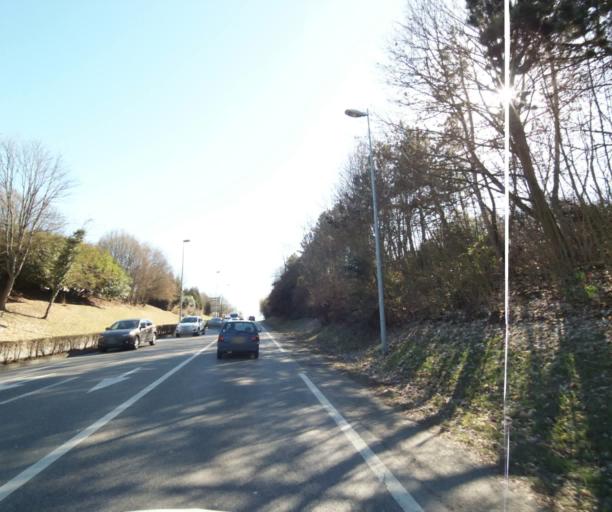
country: FR
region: Lorraine
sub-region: Departement de Meurthe-et-Moselle
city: Vandoeuvre-les-Nancy
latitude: 48.6575
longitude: 6.1779
